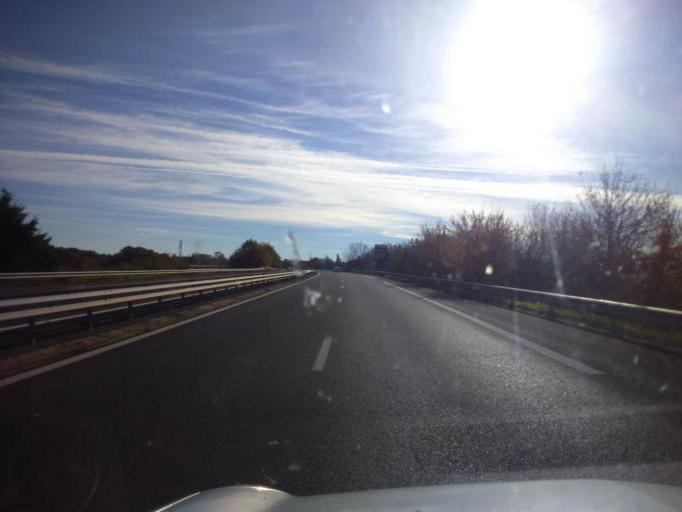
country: FR
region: Poitou-Charentes
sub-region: Departement de la Charente-Maritime
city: Breuil-Magne
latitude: 45.9686
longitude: -0.9815
